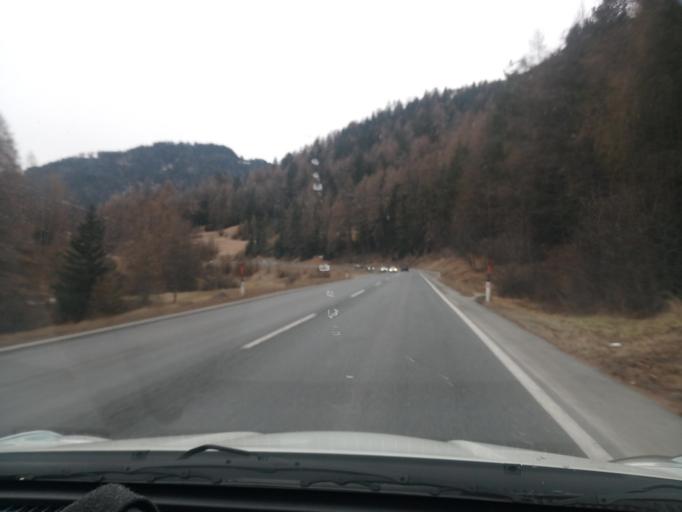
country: AT
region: Tyrol
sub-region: Politischer Bezirk Landeck
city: Nauders
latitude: 46.9038
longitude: 10.4933
